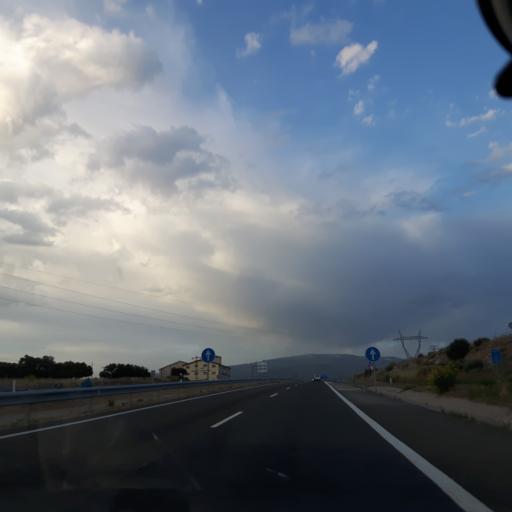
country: ES
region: Castille and Leon
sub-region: Provincia de Salamanca
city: Fuentes de Bejar
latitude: 40.4968
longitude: -5.6758
